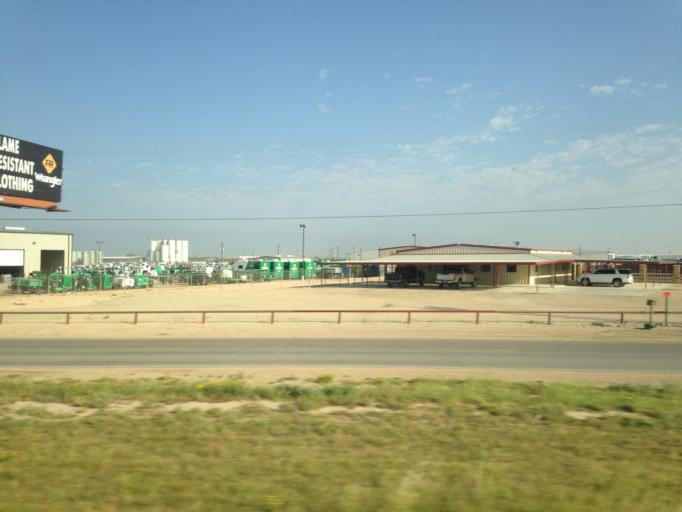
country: US
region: Texas
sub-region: Midland County
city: Midland
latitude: 31.9879
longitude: -102.0325
